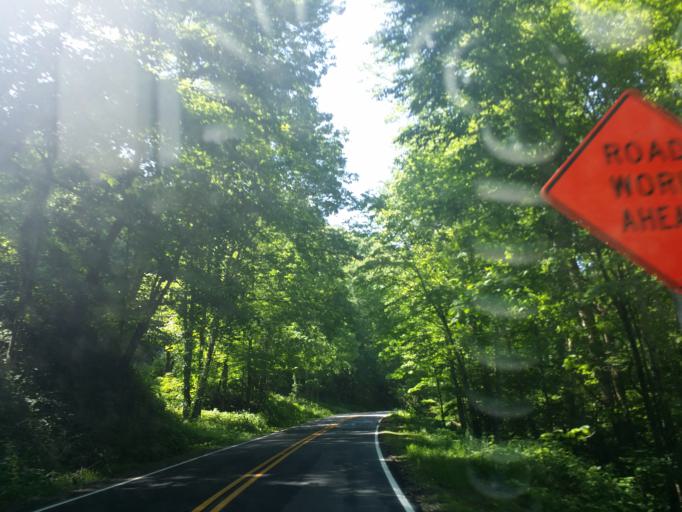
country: US
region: North Carolina
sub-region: Madison County
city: Marshall
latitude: 35.7280
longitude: -82.8410
